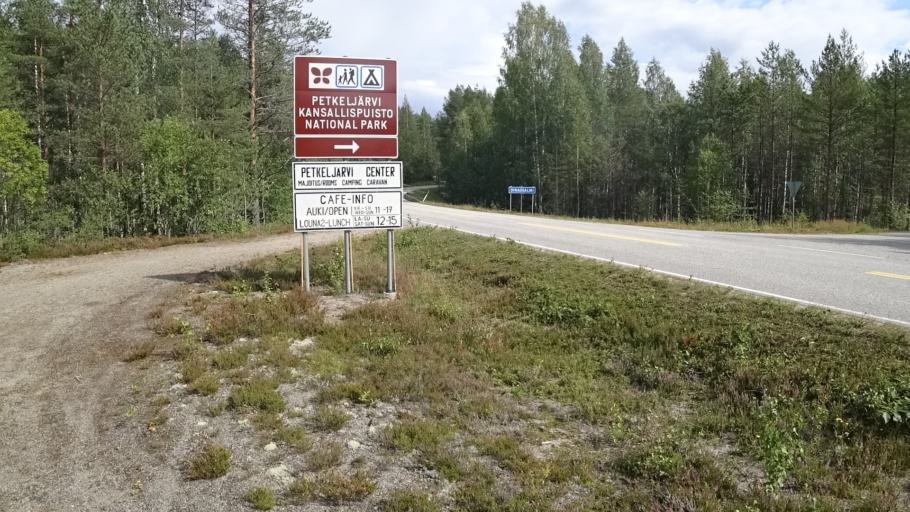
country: FI
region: North Karelia
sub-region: Joensuu
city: Ilomantsi
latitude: 62.6228
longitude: 31.1924
